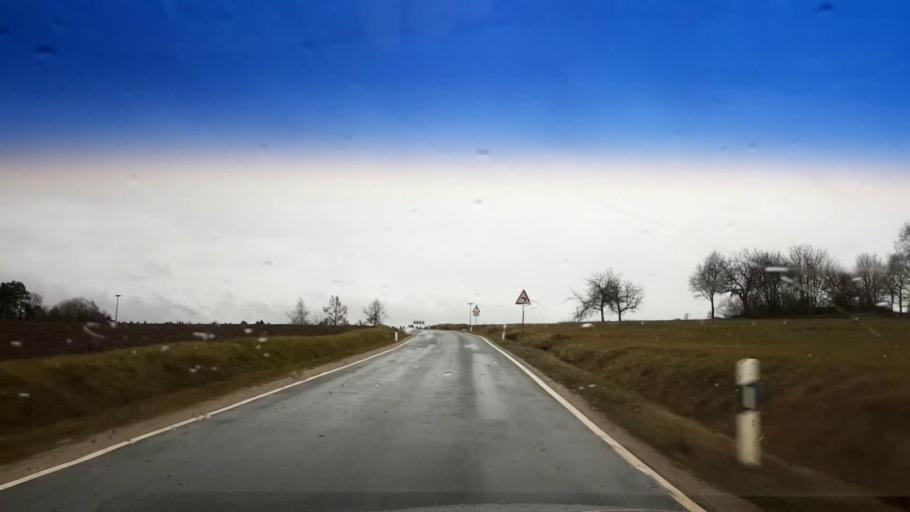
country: DE
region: Bavaria
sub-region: Upper Franconia
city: Poxdorf
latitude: 49.8969
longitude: 11.0934
